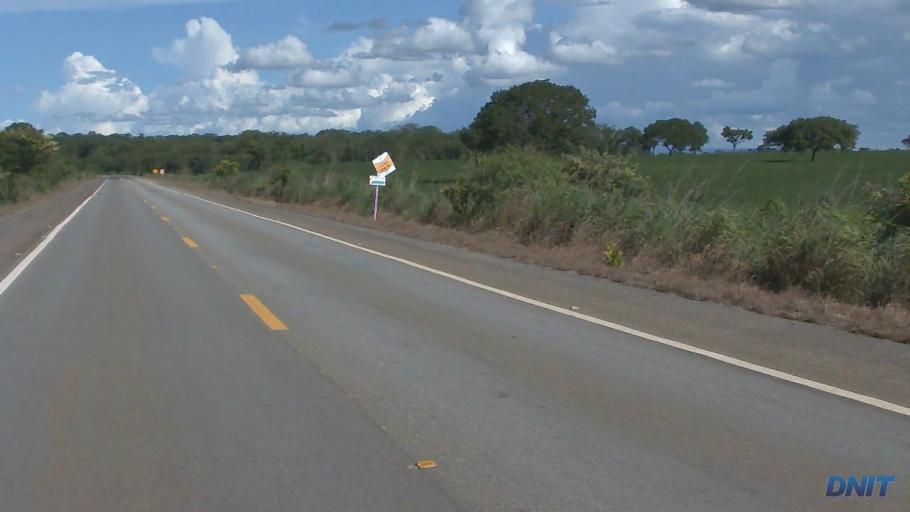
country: BR
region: Goias
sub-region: Padre Bernardo
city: Padre Bernardo
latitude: -15.2172
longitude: -48.5542
